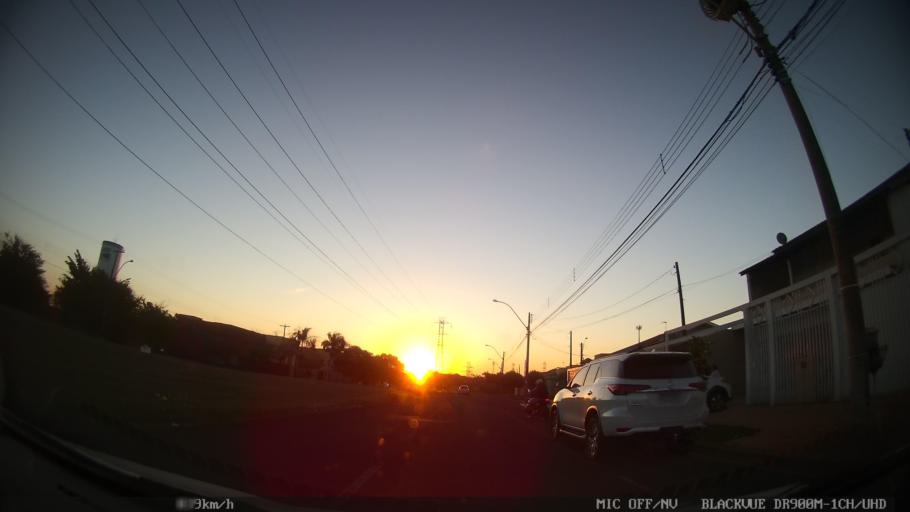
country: BR
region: Sao Paulo
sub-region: Sao Jose Do Rio Preto
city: Sao Jose do Rio Preto
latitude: -20.7991
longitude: -49.3480
